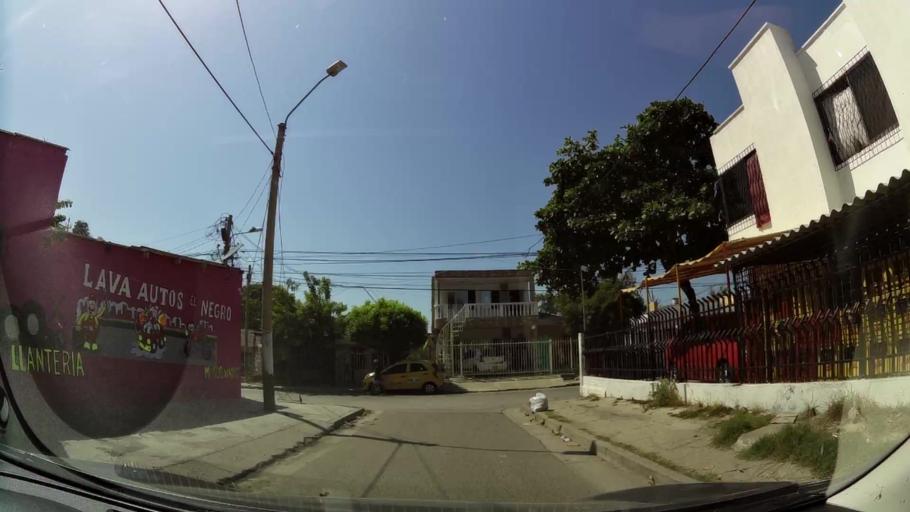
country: CO
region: Bolivar
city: Cartagena
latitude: 10.4369
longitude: -75.5208
